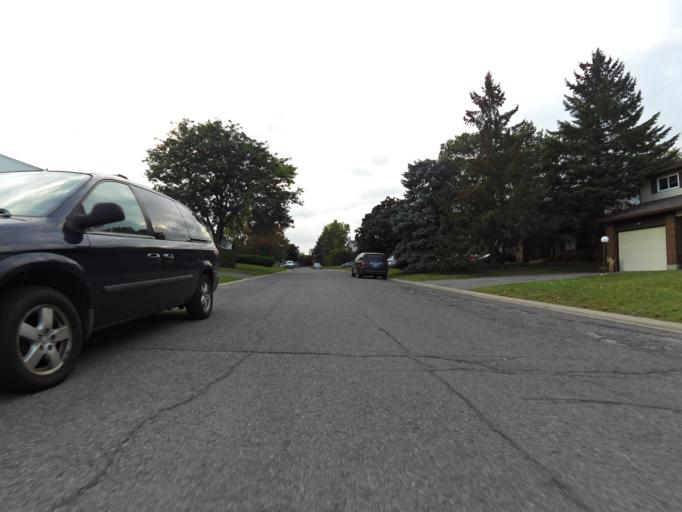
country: CA
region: Ontario
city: Bells Corners
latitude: 45.2717
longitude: -75.7552
